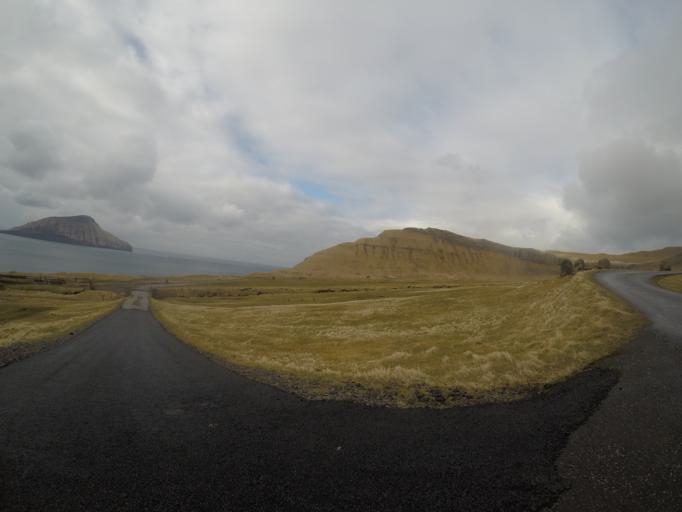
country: FO
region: Streymoy
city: Kollafjordhur
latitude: 62.0407
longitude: -6.9549
